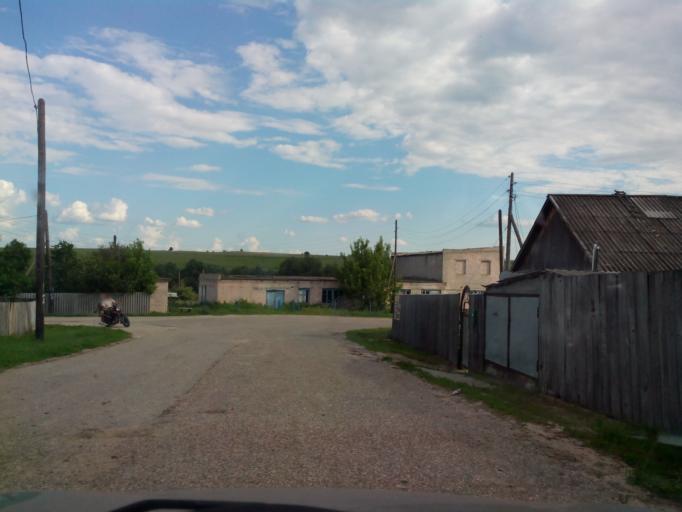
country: RU
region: Volgograd
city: Slashchevskaya
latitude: 49.7769
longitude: 42.4417
